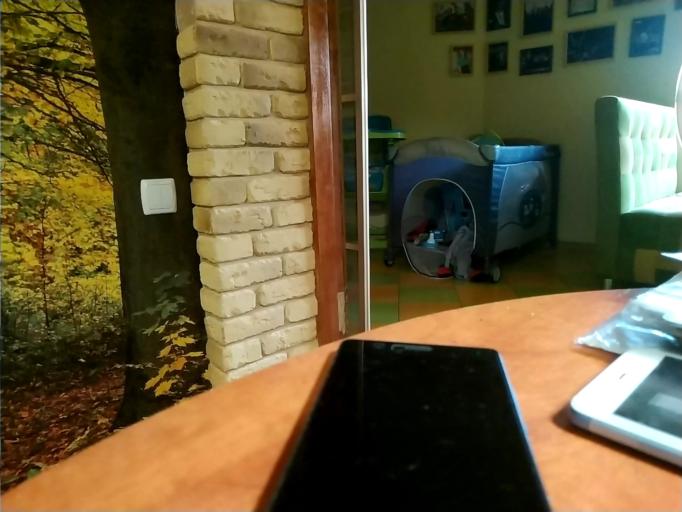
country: RU
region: Kaluga
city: Duminichi
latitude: 53.6997
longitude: 35.4315
